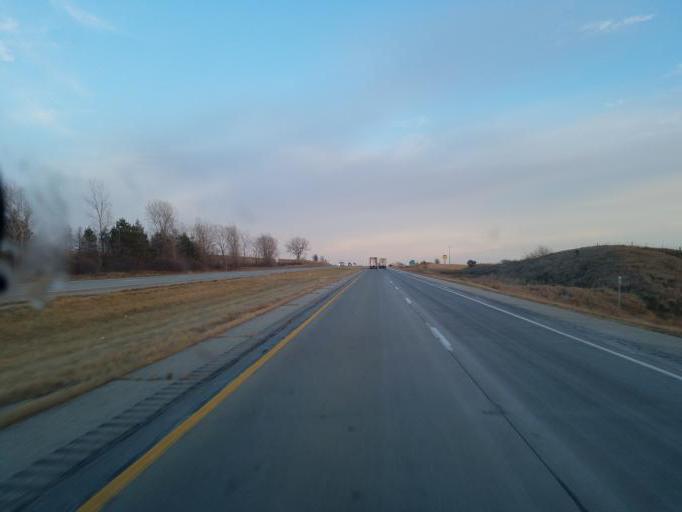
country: US
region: Iowa
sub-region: Pottawattamie County
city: Avoca
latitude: 41.4982
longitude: -95.5574
